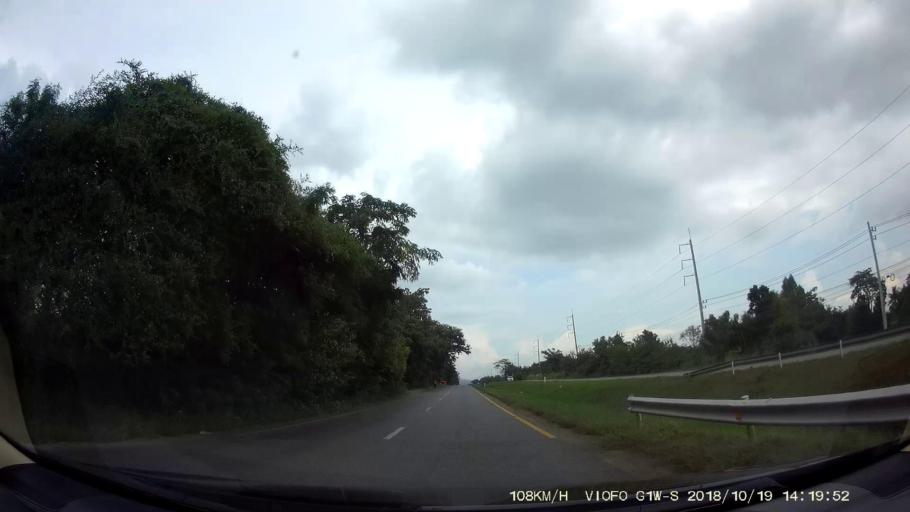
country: TH
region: Chaiyaphum
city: Kaeng Khro
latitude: 16.0334
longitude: 102.2500
